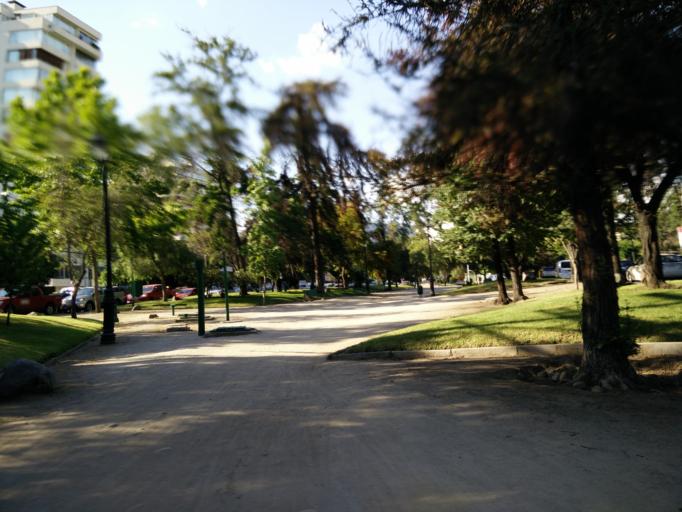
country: CL
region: Santiago Metropolitan
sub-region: Provincia de Santiago
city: Villa Presidente Frei, Nunoa, Santiago, Chile
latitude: -33.4086
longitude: -70.5873
